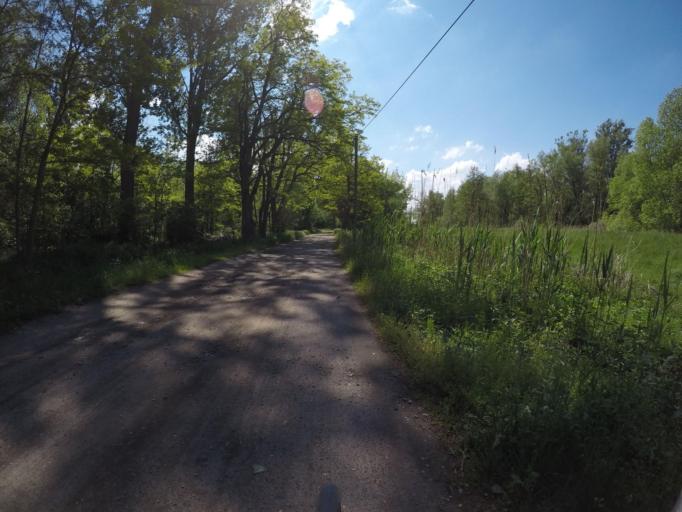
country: DE
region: Brandenburg
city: Werder
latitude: 52.4223
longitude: 12.9418
